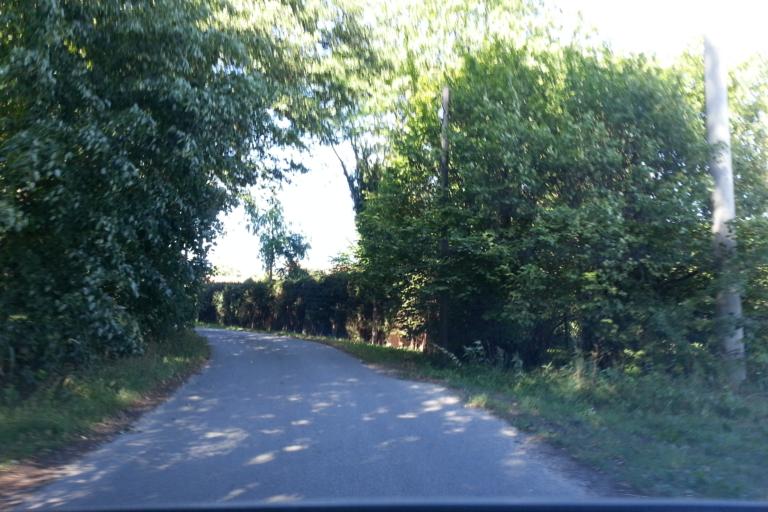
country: DE
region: Mecklenburg-Vorpommern
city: Eggesin
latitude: 53.6940
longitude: 14.0600
